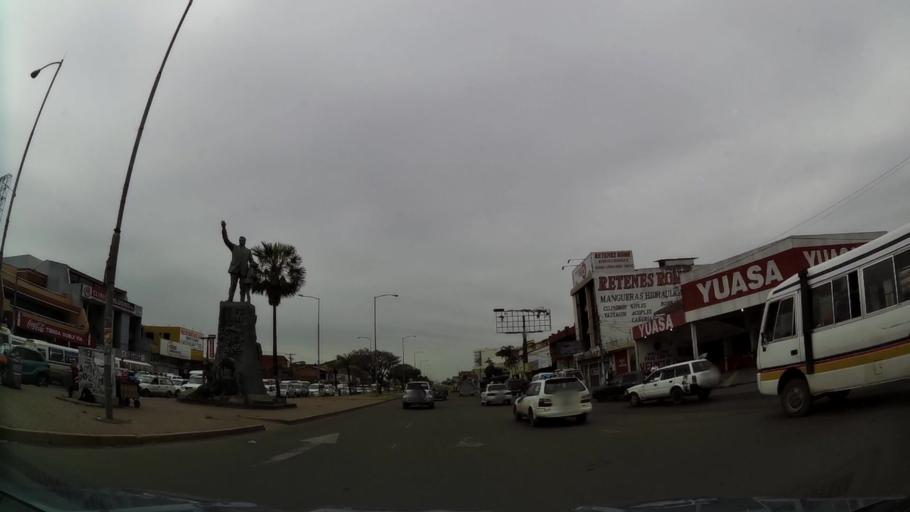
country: BO
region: Santa Cruz
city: Santa Cruz de la Sierra
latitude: -17.8038
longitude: -63.1991
